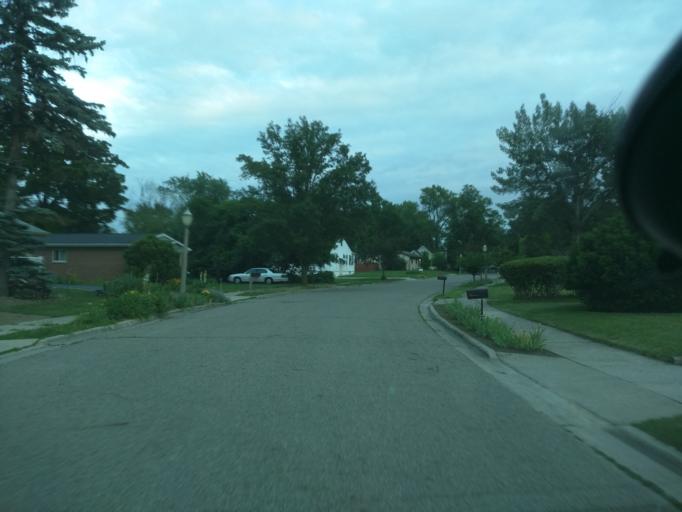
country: US
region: Michigan
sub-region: Ingham County
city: Lansing
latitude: 42.7002
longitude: -84.5839
